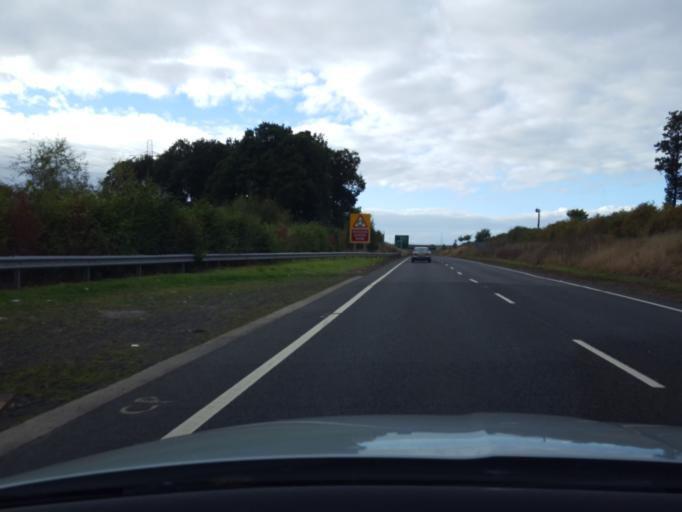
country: GB
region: Scotland
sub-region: Midlothian
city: Dalkeith
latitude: 55.9124
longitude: -3.0565
